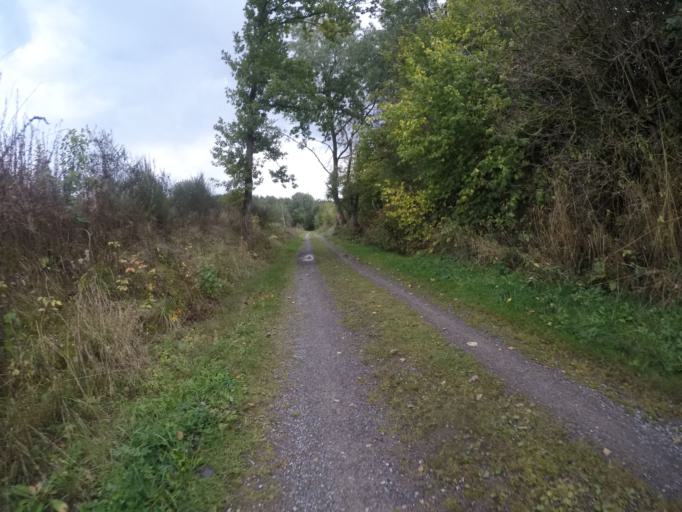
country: BE
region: Wallonia
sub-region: Province du Luxembourg
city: Fauvillers
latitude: 49.8865
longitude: 5.6757
